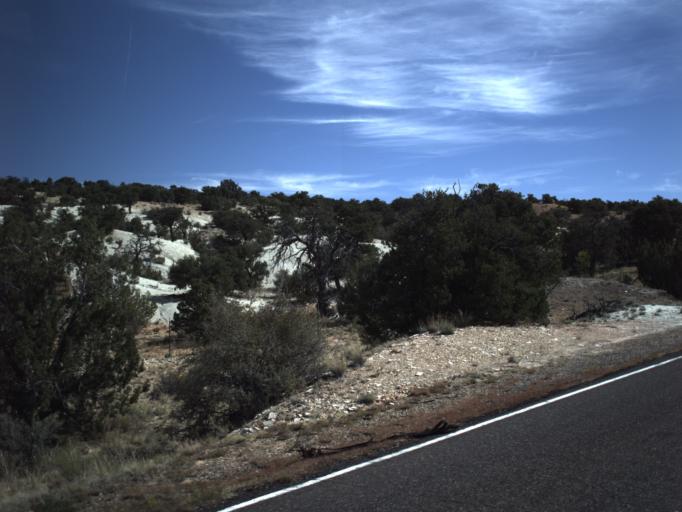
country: US
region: Utah
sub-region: Wayne County
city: Loa
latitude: 37.7406
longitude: -111.5543
